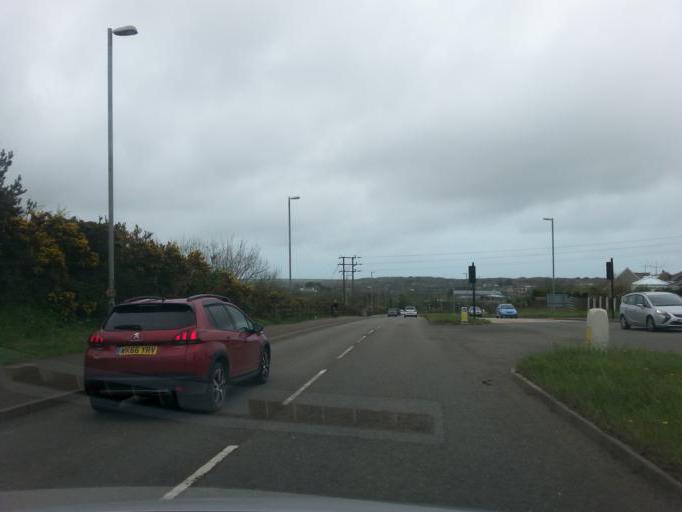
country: GB
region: England
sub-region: Cornwall
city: Camborne
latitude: 50.2268
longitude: -5.2800
